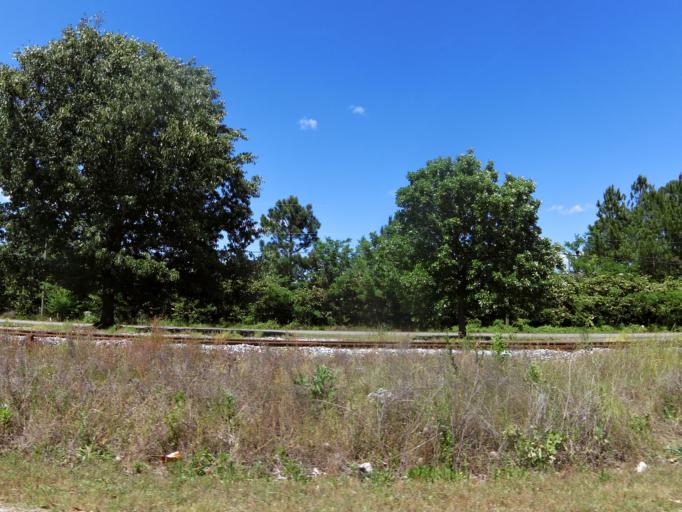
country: US
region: South Carolina
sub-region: Aiken County
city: Aiken
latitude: 33.5531
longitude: -81.7039
